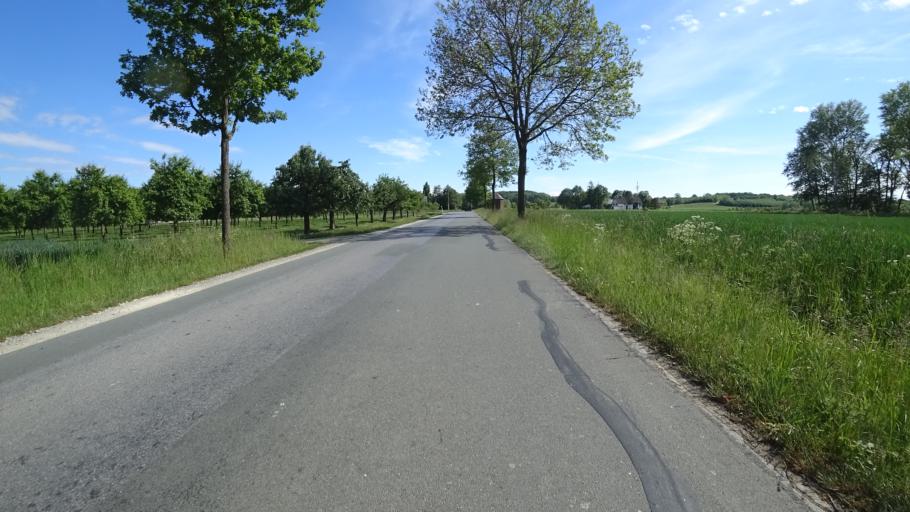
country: DE
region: North Rhine-Westphalia
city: Oelde
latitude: 51.8166
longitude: 8.2220
